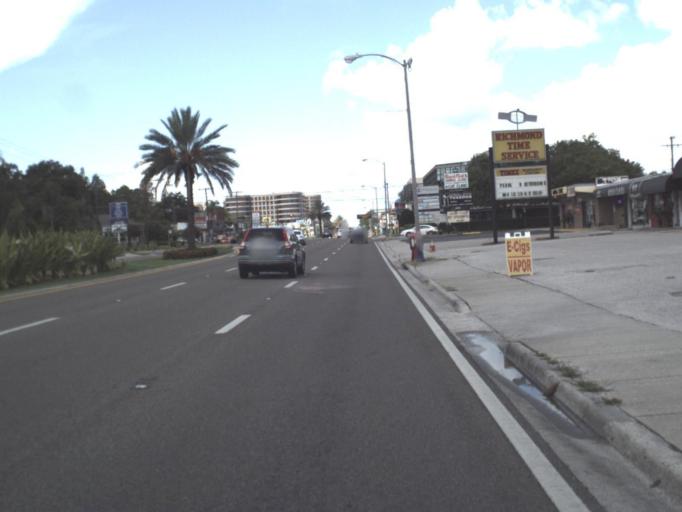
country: US
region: Florida
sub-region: Hillsborough County
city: Tampa
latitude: 27.9449
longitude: -82.5168
